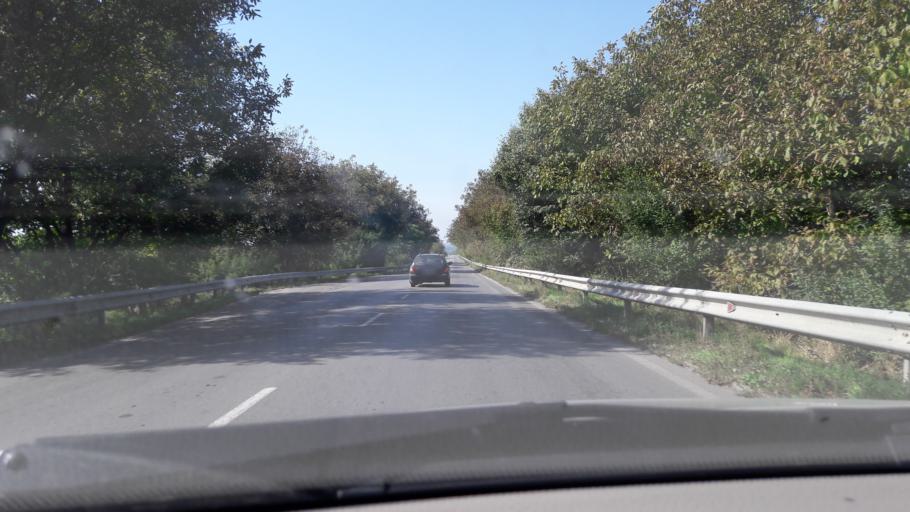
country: BG
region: Razgrad
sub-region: Obshtina Razgrad
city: Razgrad
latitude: 43.5458
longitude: 26.4926
